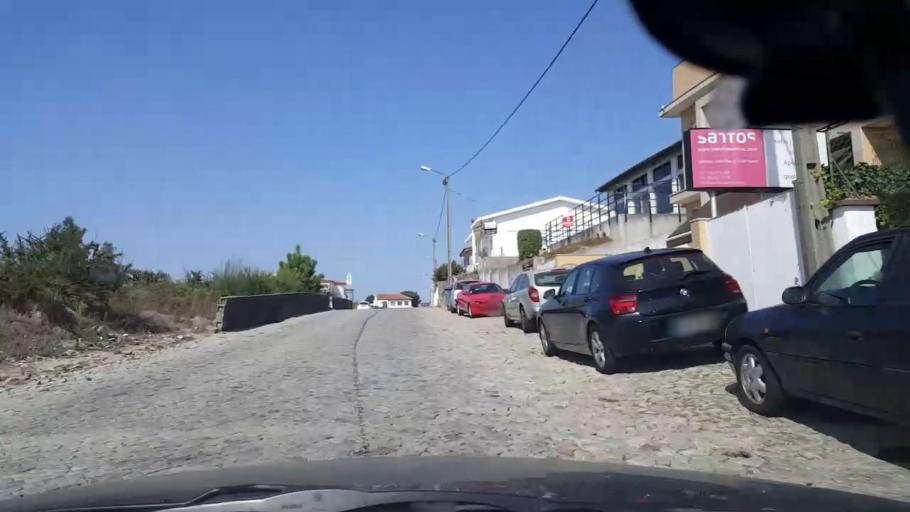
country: PT
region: Porto
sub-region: Vila do Conde
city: Arvore
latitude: 41.3777
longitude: -8.7031
